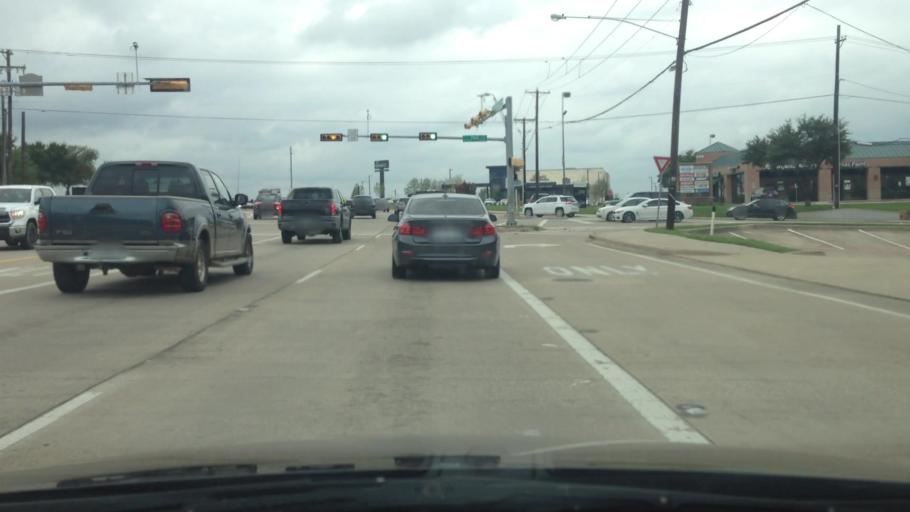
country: US
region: Texas
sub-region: Tarrant County
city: Grapevine
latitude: 32.9412
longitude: -97.0987
